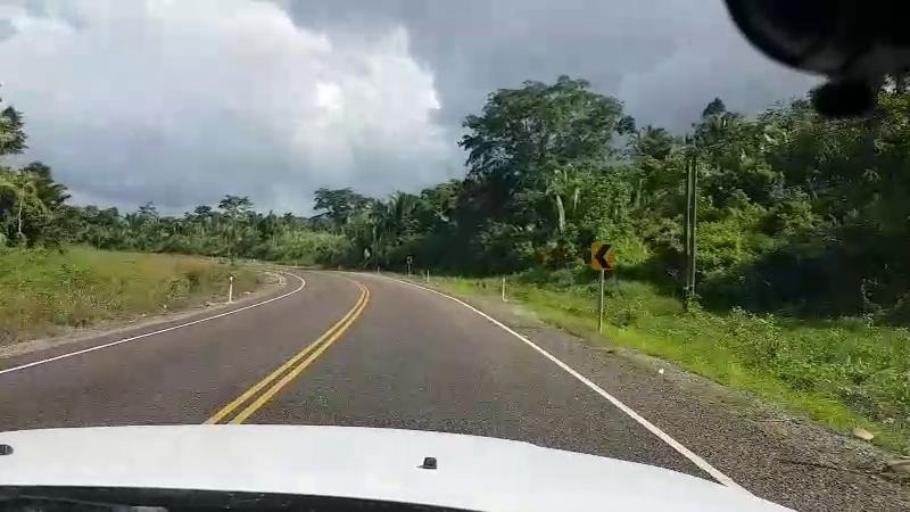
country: BZ
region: Cayo
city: Belmopan
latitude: 17.1460
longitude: -88.7309
